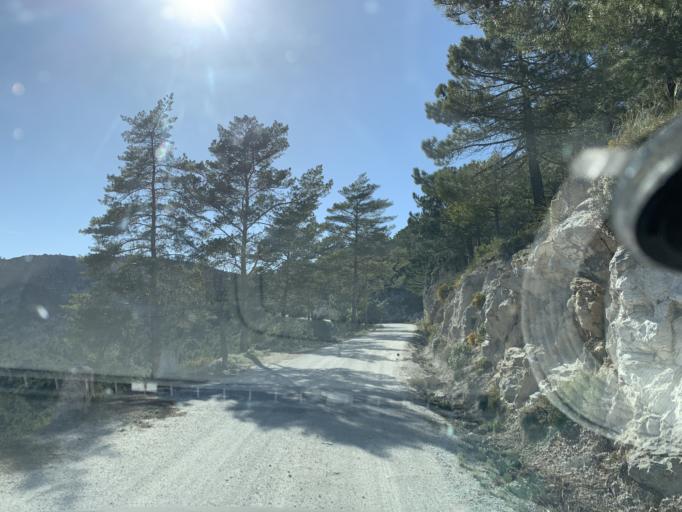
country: ES
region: Andalusia
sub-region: Provincia de Granada
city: Beas de Granada
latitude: 37.2510
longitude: -3.4611
